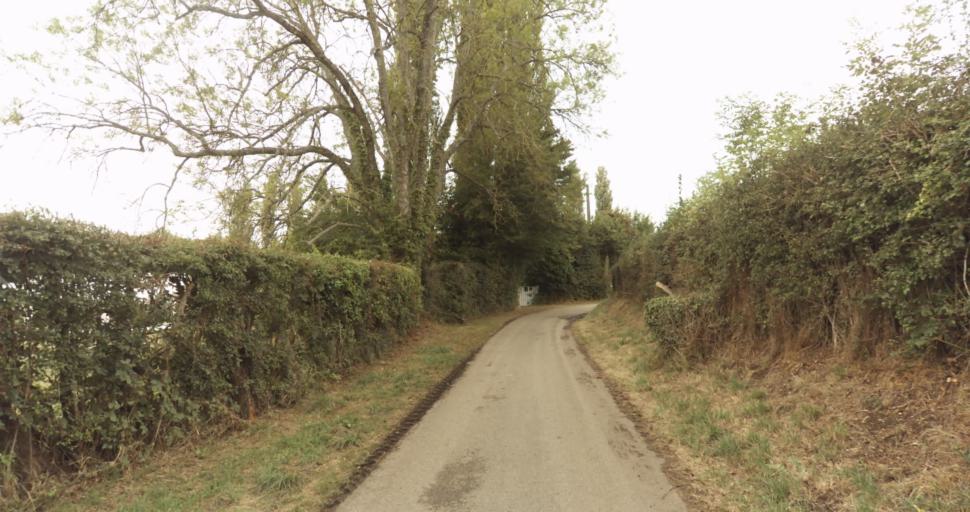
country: FR
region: Lower Normandy
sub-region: Departement de l'Orne
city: Gace
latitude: 48.8271
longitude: 0.2820
